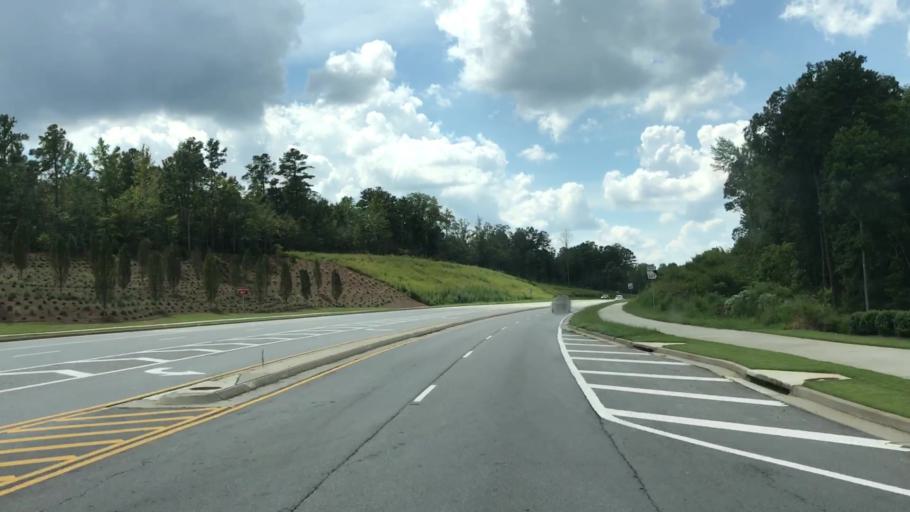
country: US
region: Georgia
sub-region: Hall County
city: Flowery Branch
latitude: 34.1109
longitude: -83.8610
